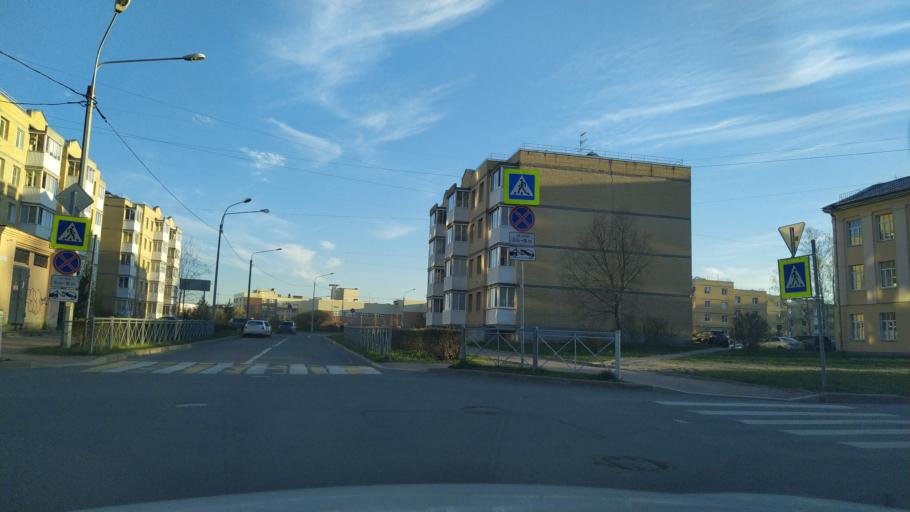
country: RU
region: St.-Petersburg
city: Pushkin
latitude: 59.7074
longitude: 30.3846
